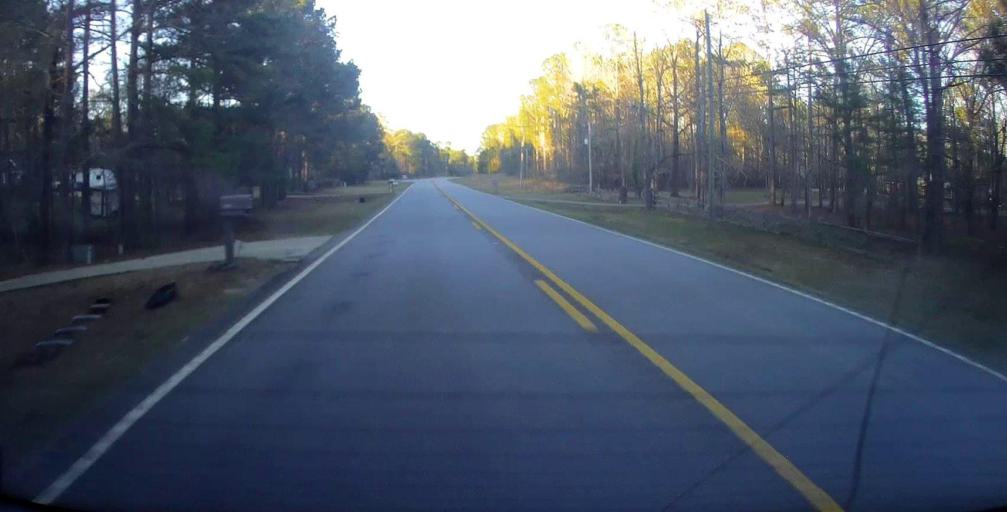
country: US
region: Alabama
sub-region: Lee County
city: Smiths Station
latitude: 32.6432
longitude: -85.0210
